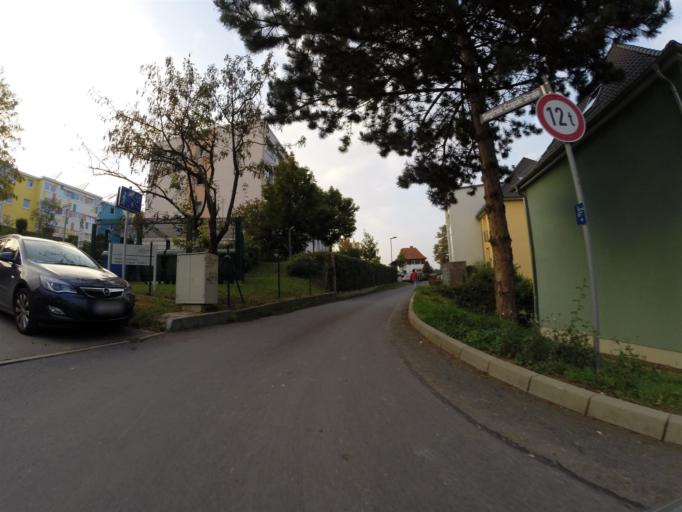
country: DE
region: Thuringia
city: Jena
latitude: 50.9203
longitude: 11.5659
